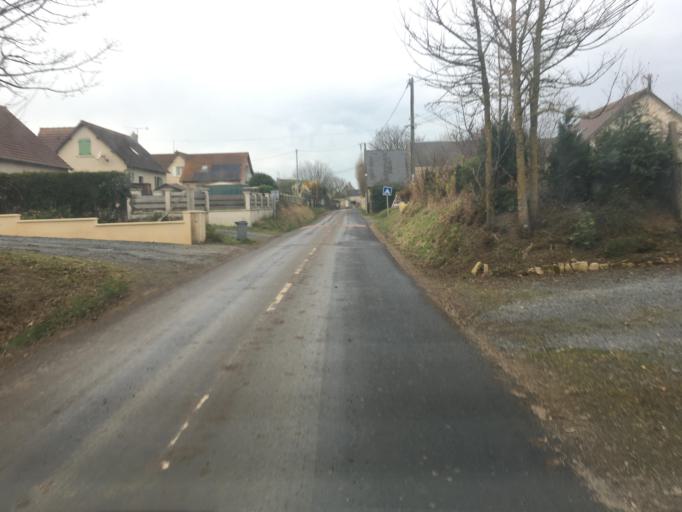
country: FR
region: Lower Normandy
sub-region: Departement du Calvados
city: Saint-Vigor-le-Grand
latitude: 49.3353
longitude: -0.6397
